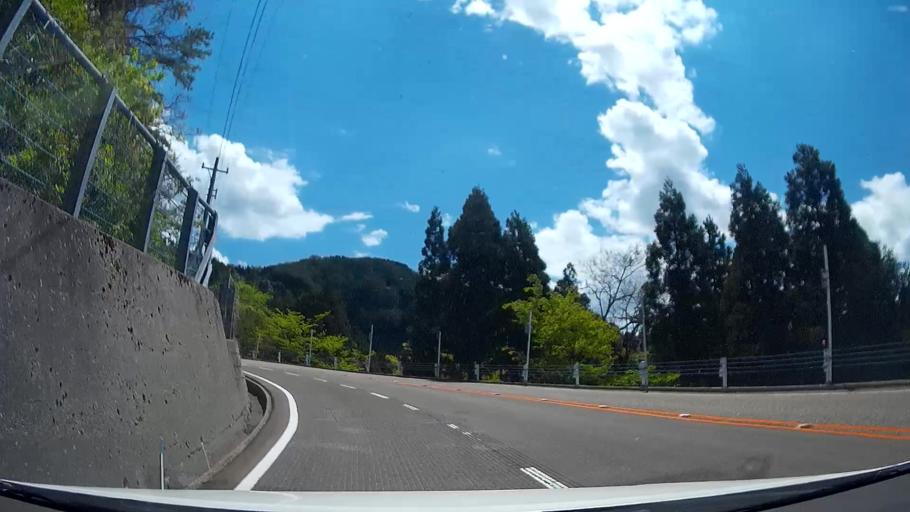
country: JP
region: Toyama
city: Fukumitsu
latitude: 36.4796
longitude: 136.8936
